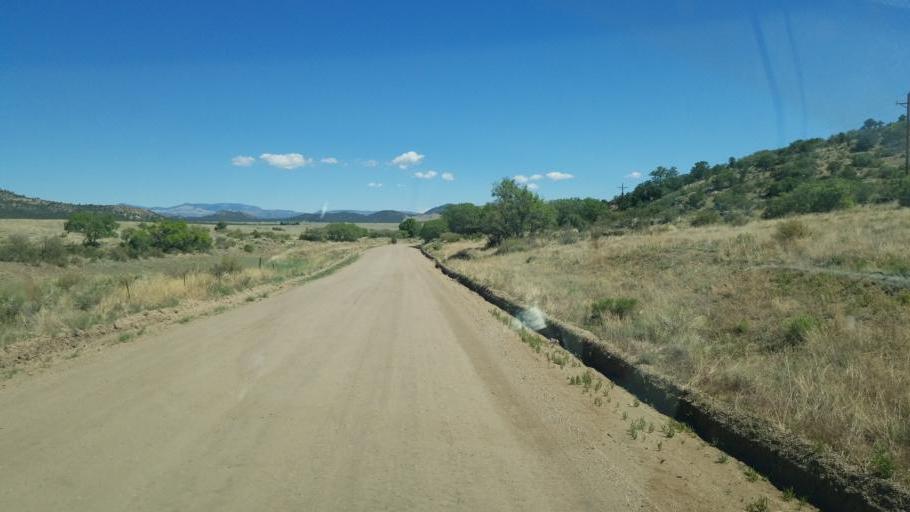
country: US
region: Colorado
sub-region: Custer County
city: Westcliffe
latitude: 38.2428
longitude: -105.5011
